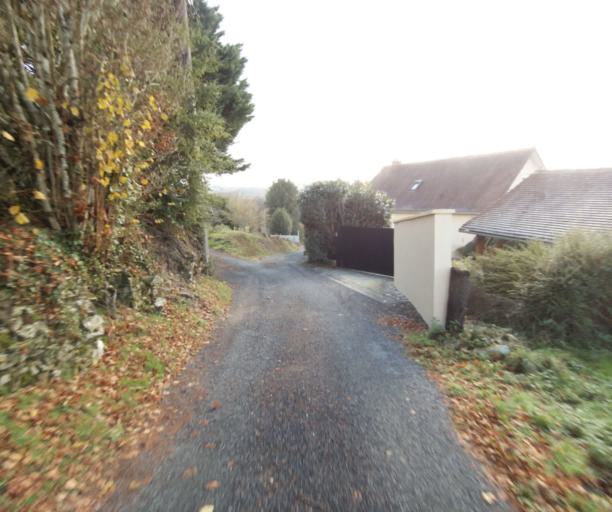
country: FR
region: Limousin
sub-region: Departement de la Correze
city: Cornil
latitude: 45.2233
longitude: 1.6882
